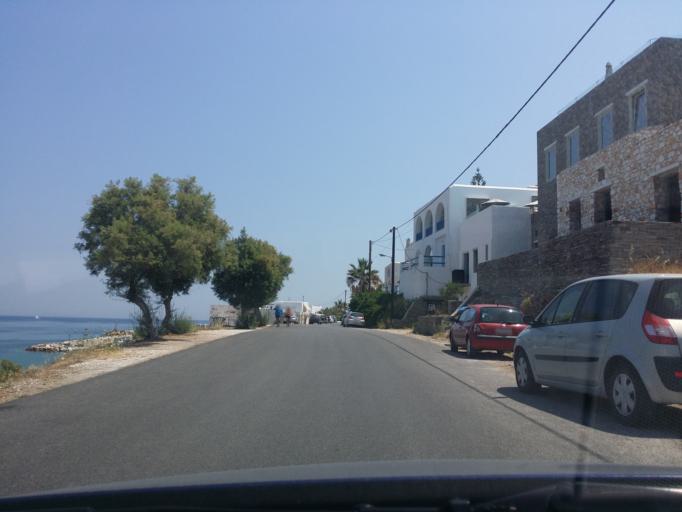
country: GR
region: South Aegean
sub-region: Nomos Kykladon
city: Naousa
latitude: 37.1221
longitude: 25.2334
